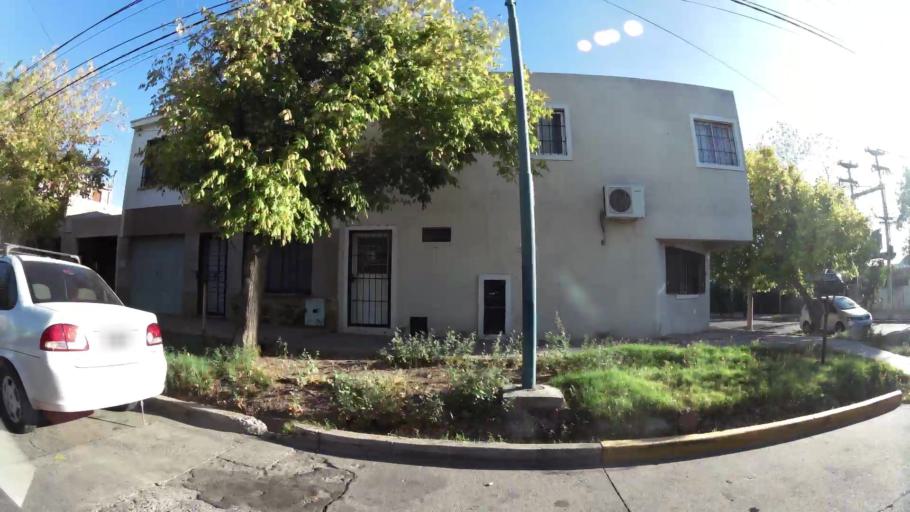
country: AR
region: Mendoza
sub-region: Departamento de Godoy Cruz
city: Godoy Cruz
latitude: -32.9276
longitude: -68.8411
